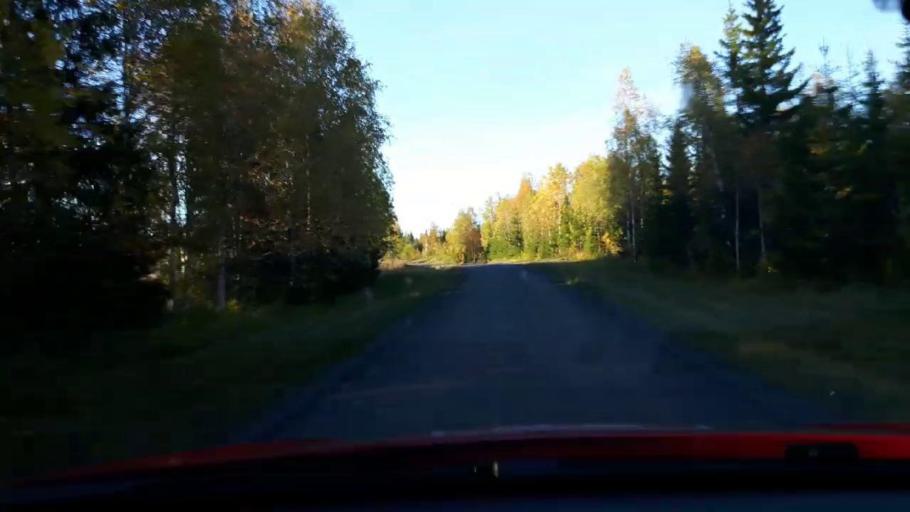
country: SE
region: Jaemtland
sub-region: Krokoms Kommun
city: Krokom
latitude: 63.4275
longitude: 14.6104
